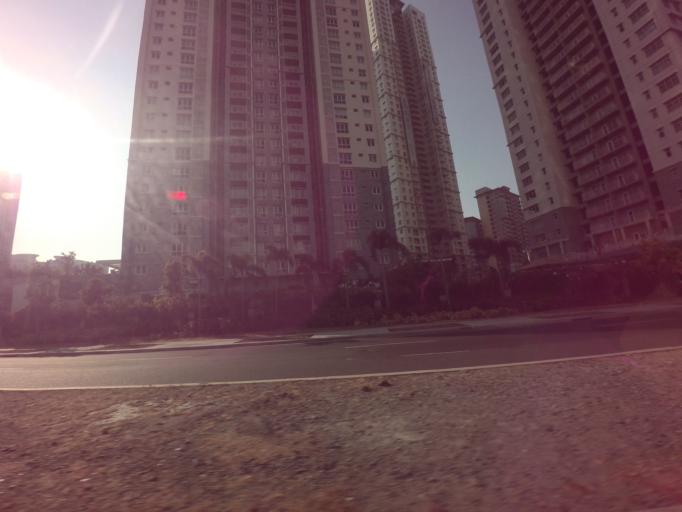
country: PH
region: Metro Manila
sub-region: Makati City
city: Makati City
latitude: 14.5458
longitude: 121.0528
